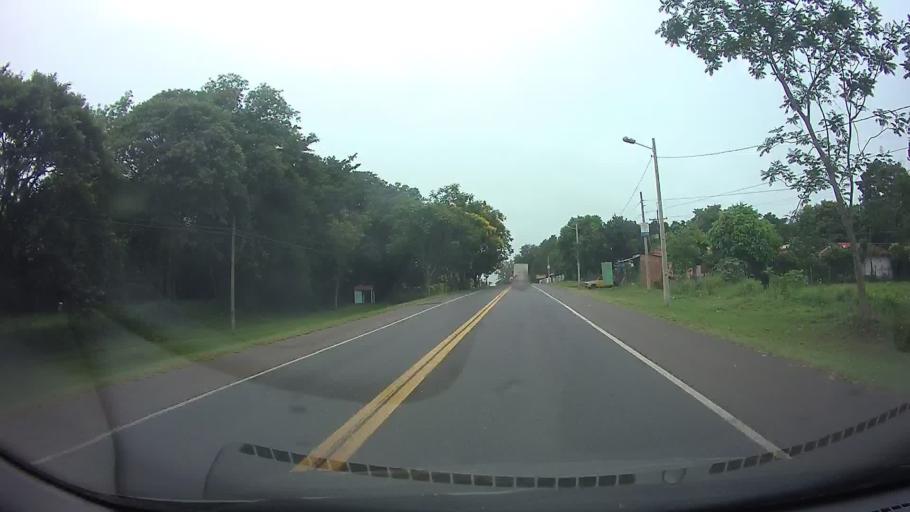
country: PY
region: Paraguari
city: Yaguaron
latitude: -25.5864
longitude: -57.2379
